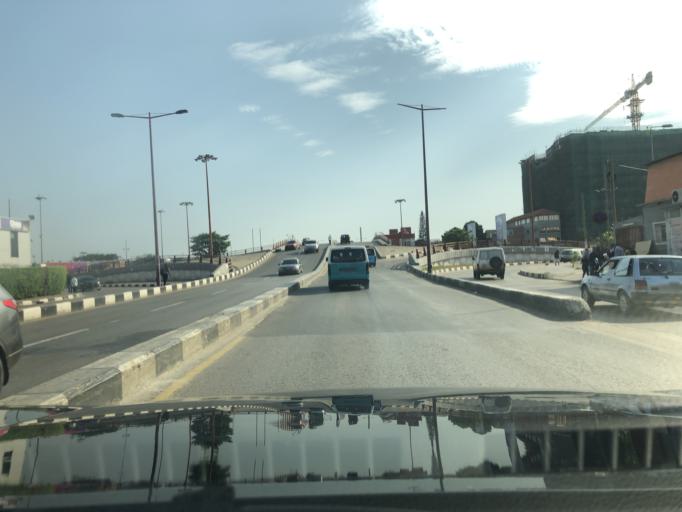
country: AO
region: Luanda
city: Luanda
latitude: -8.8452
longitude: 13.2351
